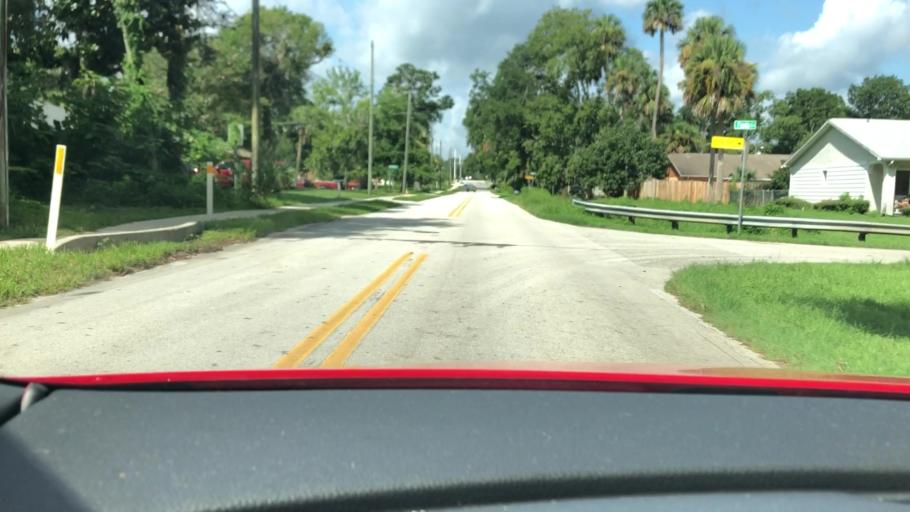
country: US
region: Florida
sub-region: Volusia County
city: Holly Hill
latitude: 29.2547
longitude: -81.0684
